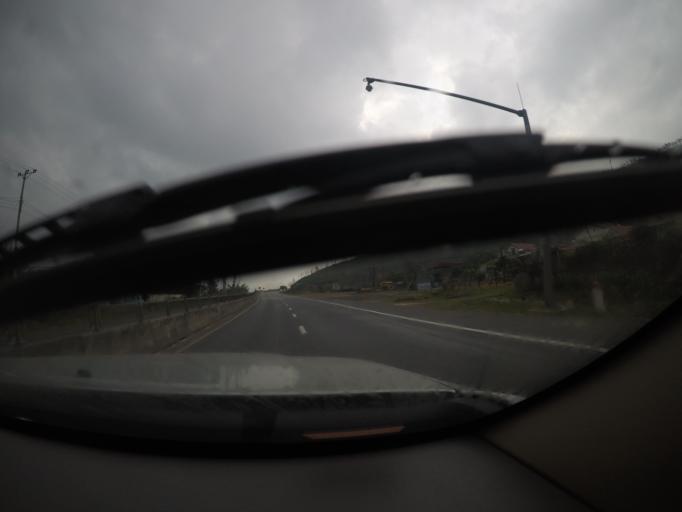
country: VN
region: Ha Tinh
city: Ky Anh
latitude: 17.9872
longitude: 106.4780
